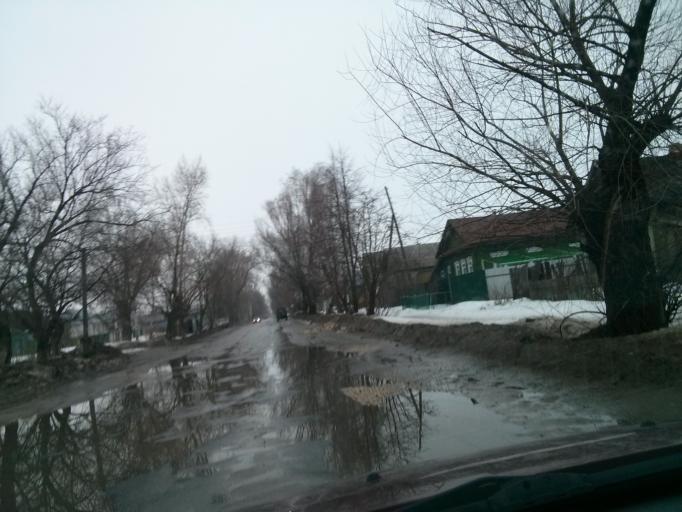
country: RU
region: Nizjnij Novgorod
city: Shimorskoye
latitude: 55.3360
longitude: 41.9283
